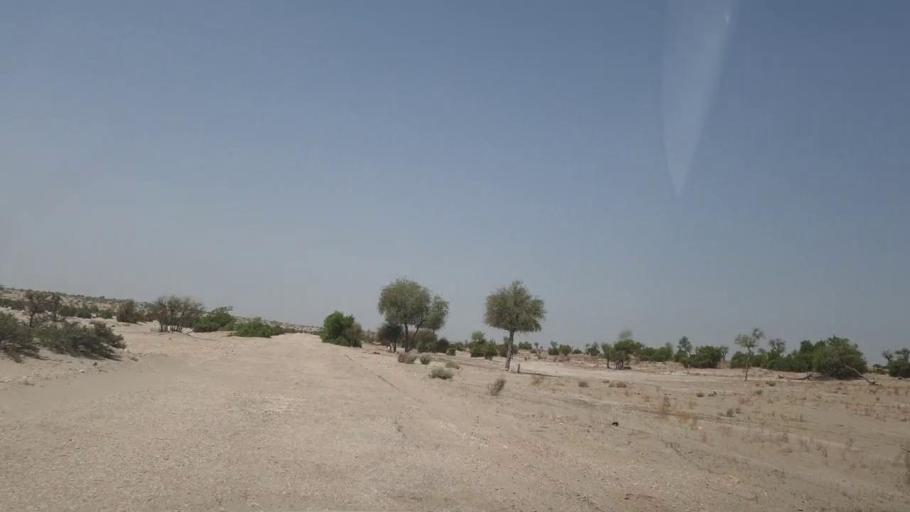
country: PK
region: Sindh
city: Khanpur
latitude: 27.3377
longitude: 69.3127
